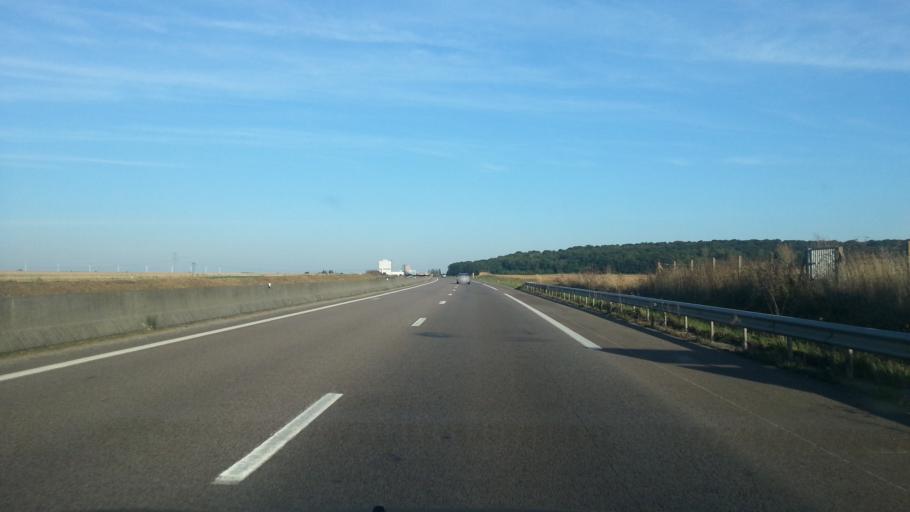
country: FR
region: Picardie
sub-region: Departement de l'Oise
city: Bailleul-sur-Therain
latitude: 49.4119
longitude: 2.2007
